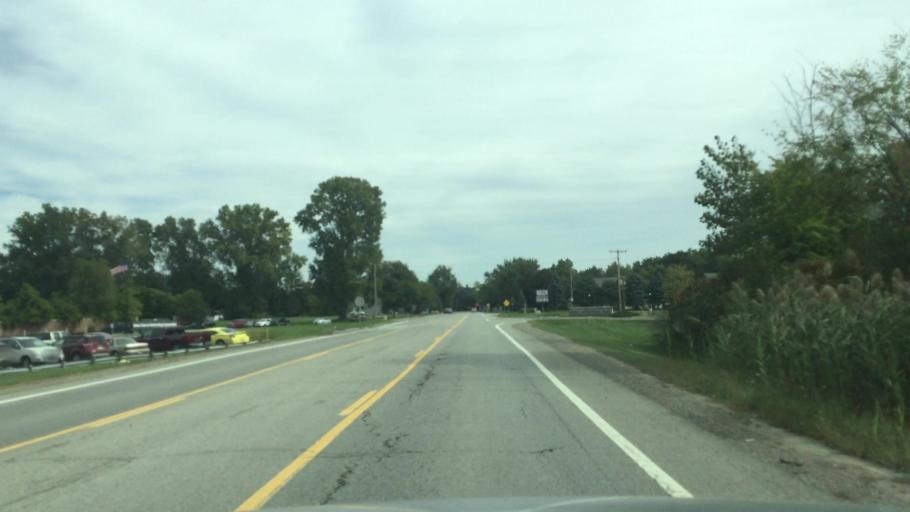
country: US
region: Michigan
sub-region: Oakland County
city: Holly
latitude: 42.8071
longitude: -83.6226
